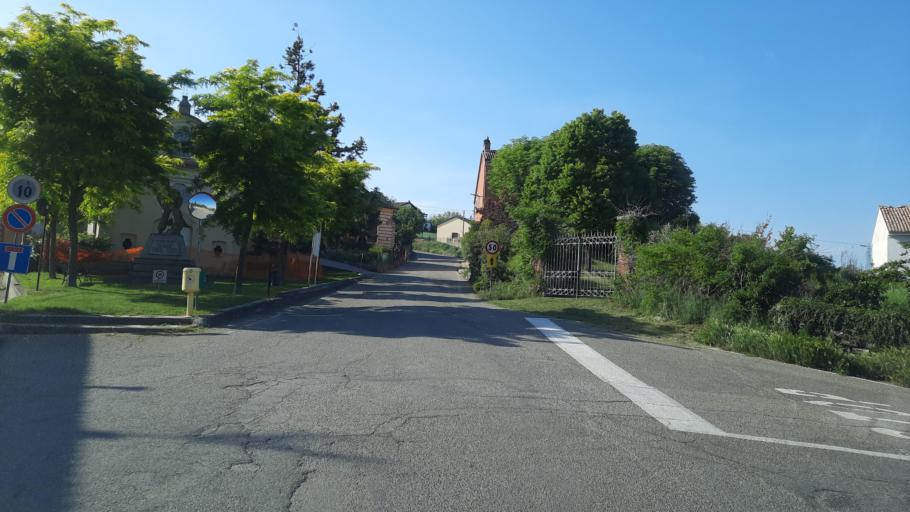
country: IT
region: Piedmont
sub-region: Provincia di Alessandria
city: San Giorgio
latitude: 45.1094
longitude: 8.4122
